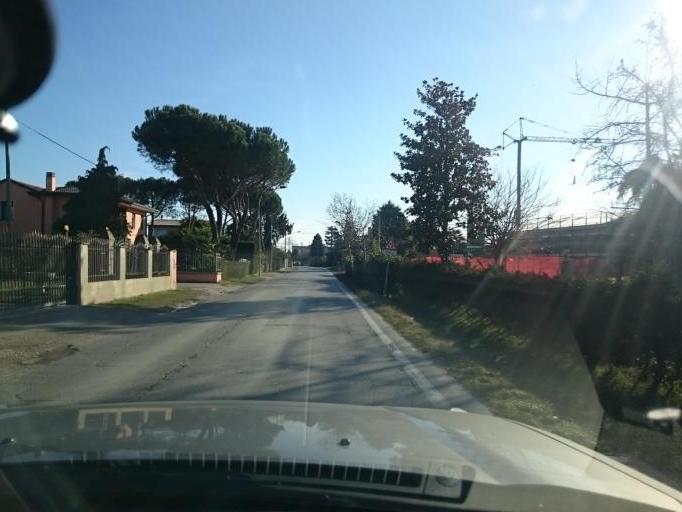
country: IT
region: Veneto
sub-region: Provincia di Venezia
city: Vigonovo
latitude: 45.3776
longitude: 11.9988
